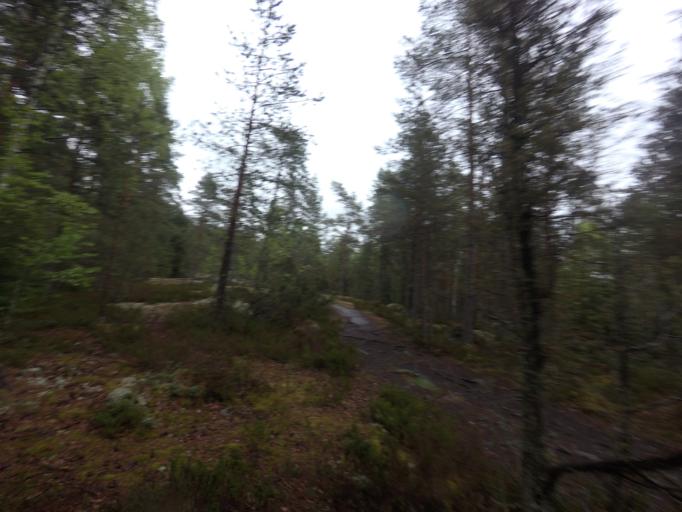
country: FI
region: Uusimaa
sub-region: Helsinki
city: Kauniainen
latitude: 60.1864
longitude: 24.7073
